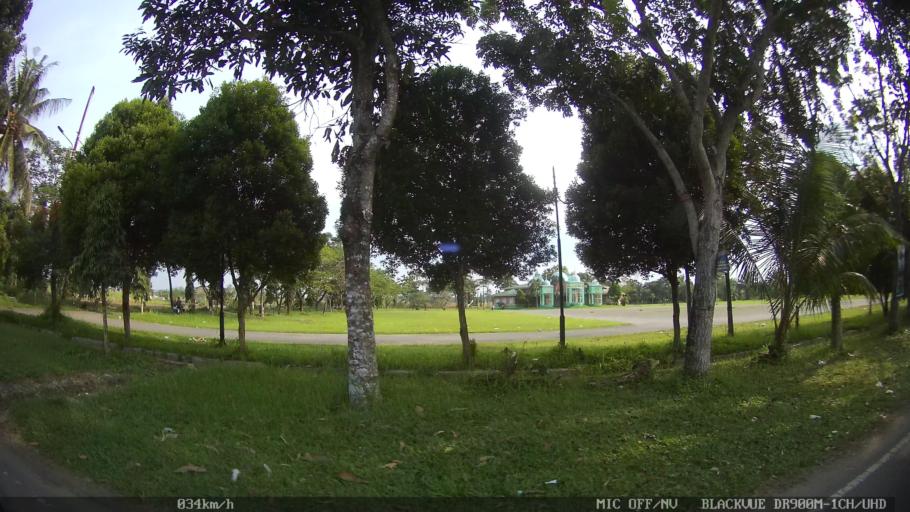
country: ID
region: North Sumatra
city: Binjai
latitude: 3.6029
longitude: 98.5034
